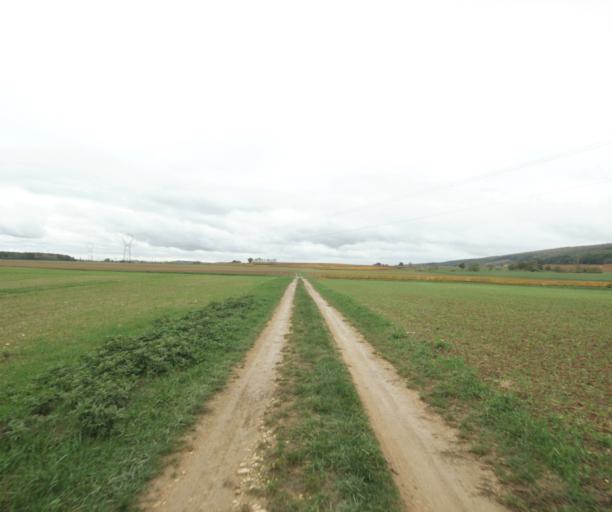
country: FR
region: Bourgogne
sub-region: Departement de Saone-et-Loire
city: Saint-Martin-Belle-Roche
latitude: 46.4659
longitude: 4.8594
